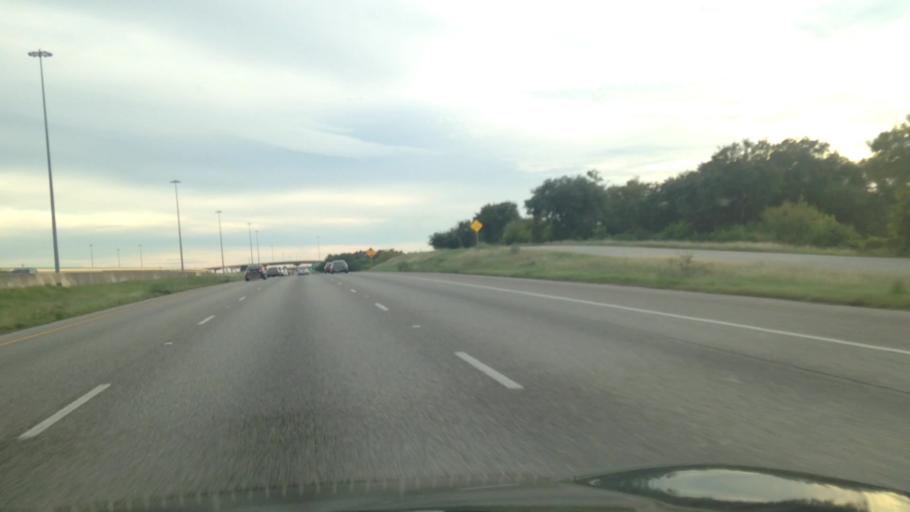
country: US
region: Texas
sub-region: Travis County
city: Onion Creek
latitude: 30.1229
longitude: -97.8029
